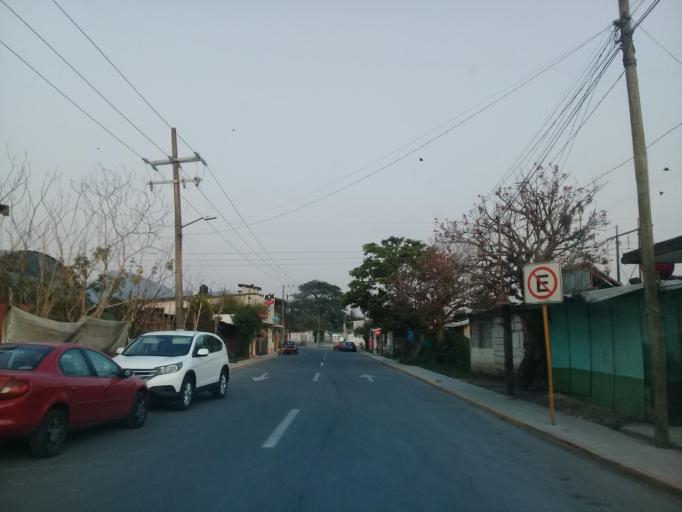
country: MX
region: Veracruz
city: Ixtac Zoquitlan
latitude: 18.8519
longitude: -97.0547
